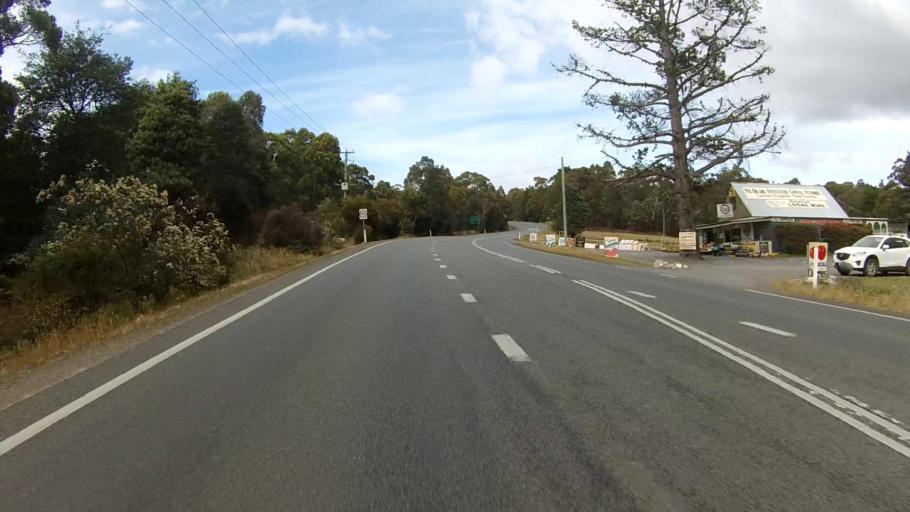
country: AU
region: Tasmania
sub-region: Kingborough
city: Kettering
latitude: -43.1068
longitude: 147.2445
